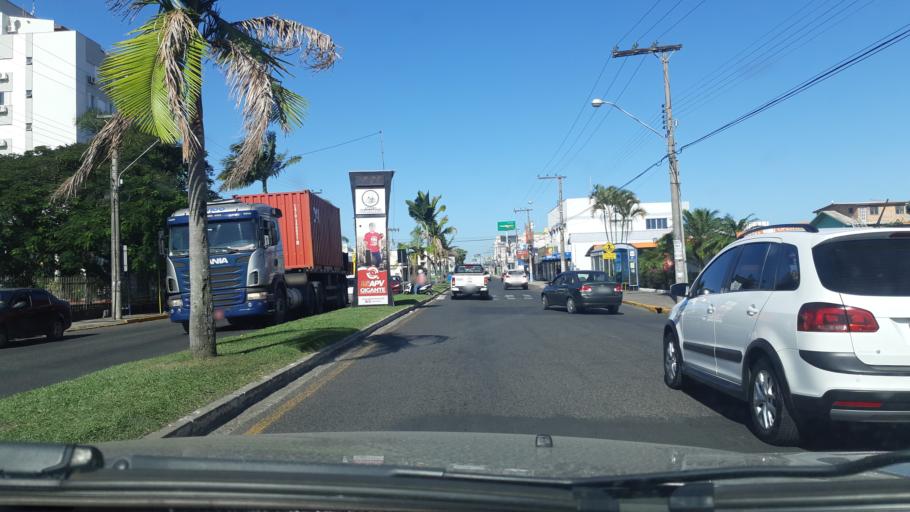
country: BR
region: Santa Catarina
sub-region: Ararangua
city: Ararangua
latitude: -28.9408
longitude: -49.4959
